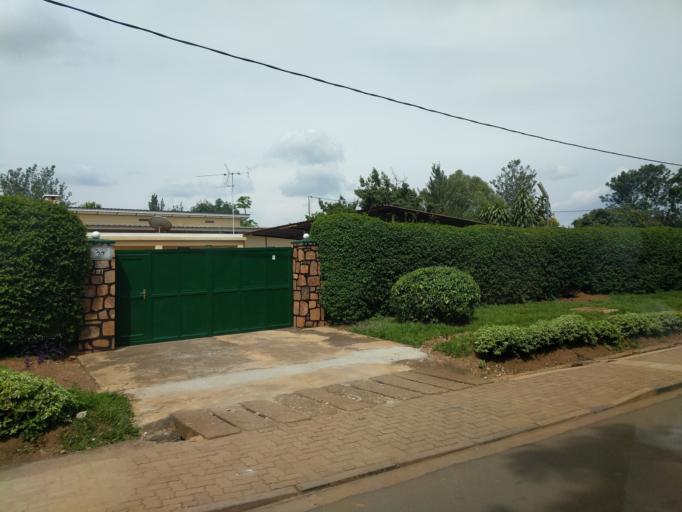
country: RW
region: Kigali
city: Kigali
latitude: -1.9768
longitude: 30.1102
